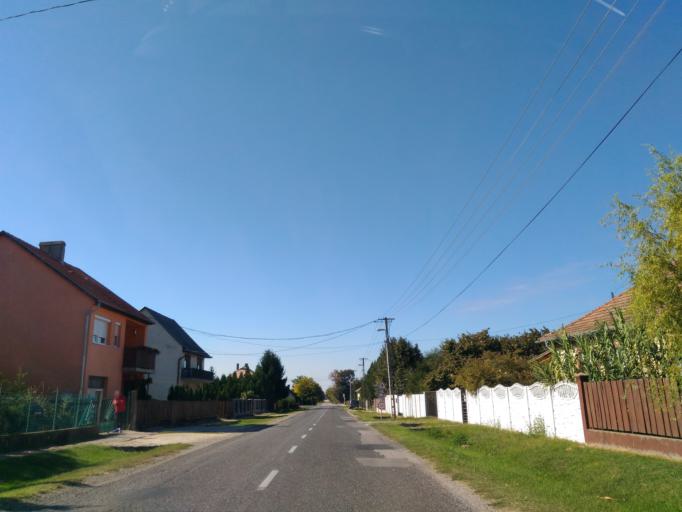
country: HU
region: Fejer
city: Ivancsa
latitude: 47.1559
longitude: 18.8241
